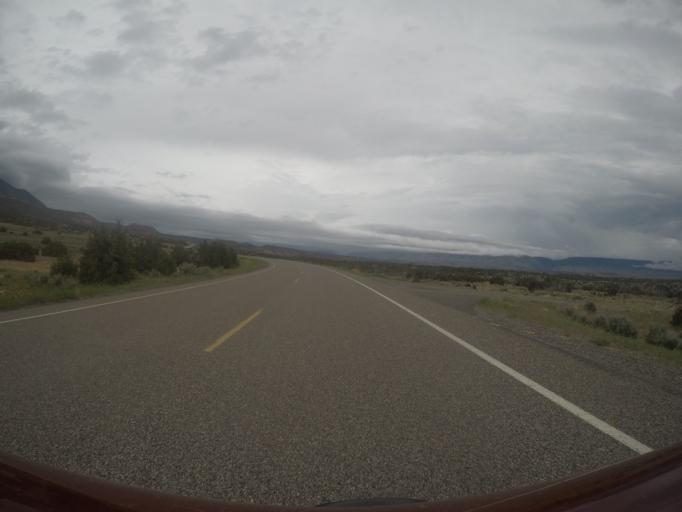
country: US
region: Wyoming
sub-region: Big Horn County
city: Lovell
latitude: 45.0848
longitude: -108.2520
